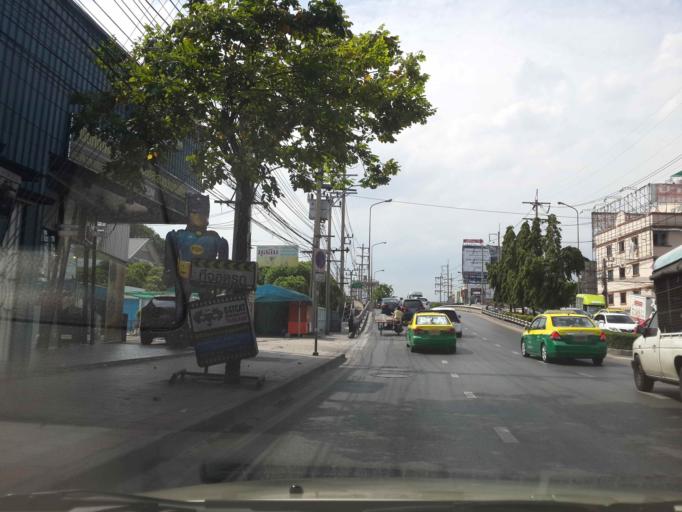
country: TH
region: Bangkok
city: Bang Kapi
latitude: 13.7639
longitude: 100.6455
